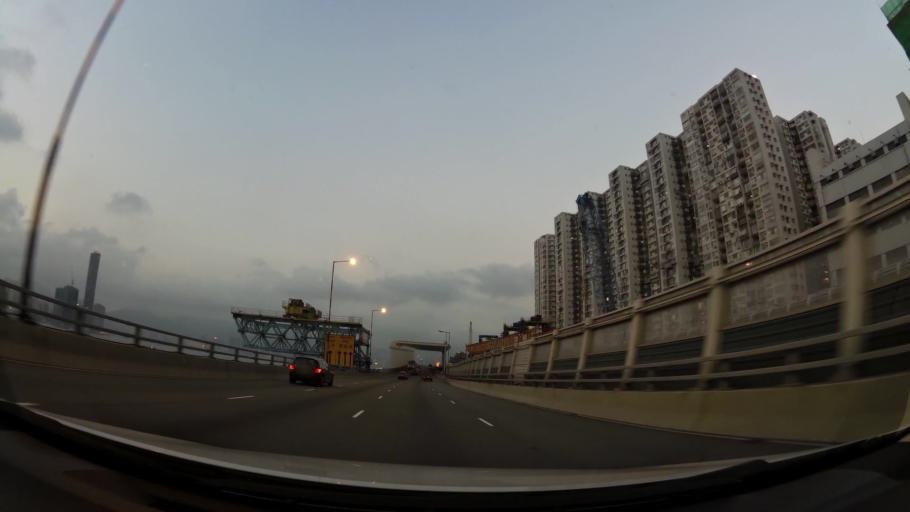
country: HK
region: Wanchai
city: Wan Chai
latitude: 22.2908
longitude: 114.1920
